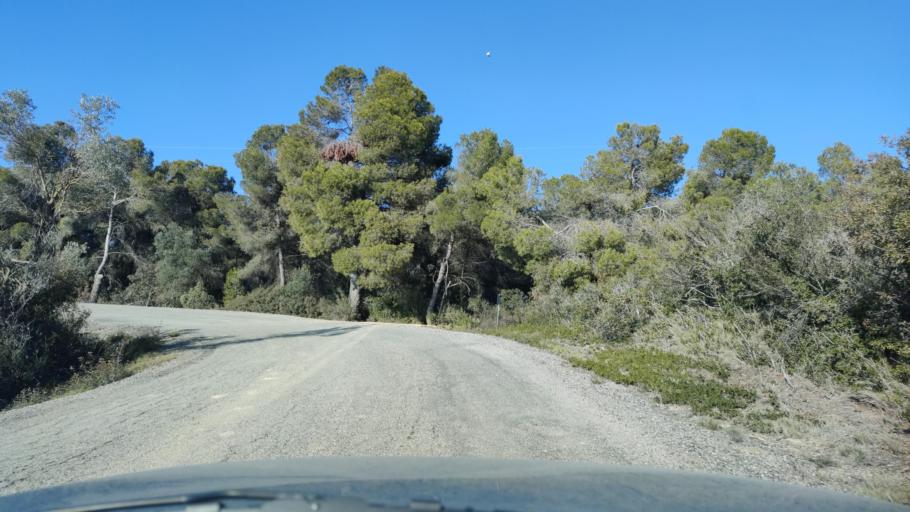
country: ES
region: Catalonia
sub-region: Provincia de Lleida
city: Torrebesses
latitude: 41.3892
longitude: 0.5648
